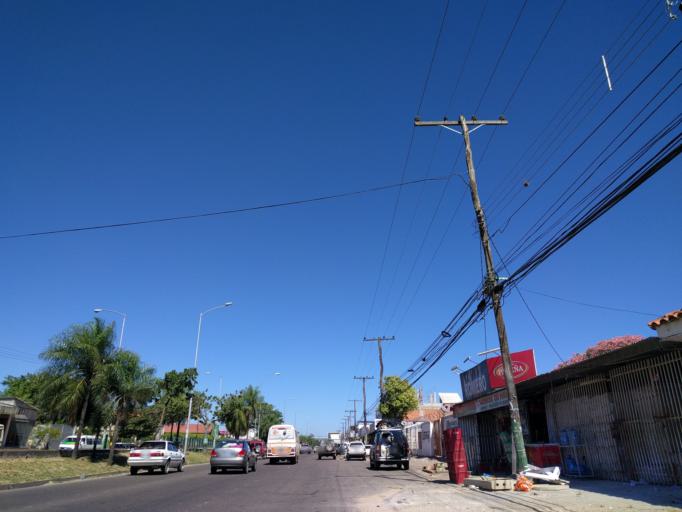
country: BO
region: Santa Cruz
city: Santa Cruz de la Sierra
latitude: -17.8253
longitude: -63.2235
